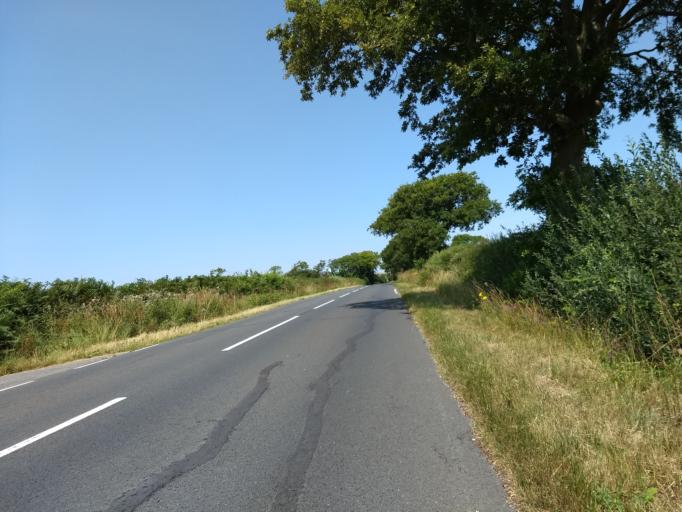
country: GB
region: England
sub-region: Isle of Wight
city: Northwood
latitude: 50.7207
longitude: -1.3530
